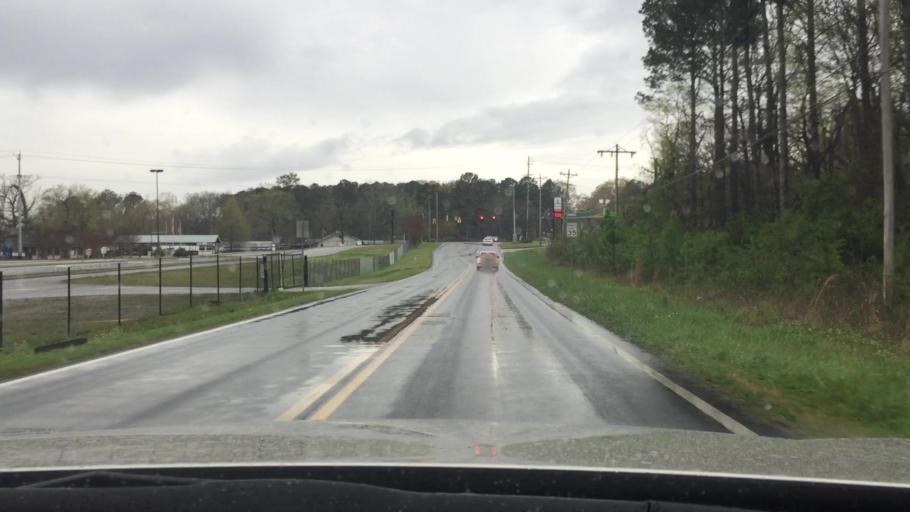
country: US
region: Georgia
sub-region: Catoosa County
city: Lakeview
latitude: 34.9771
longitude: -85.2424
